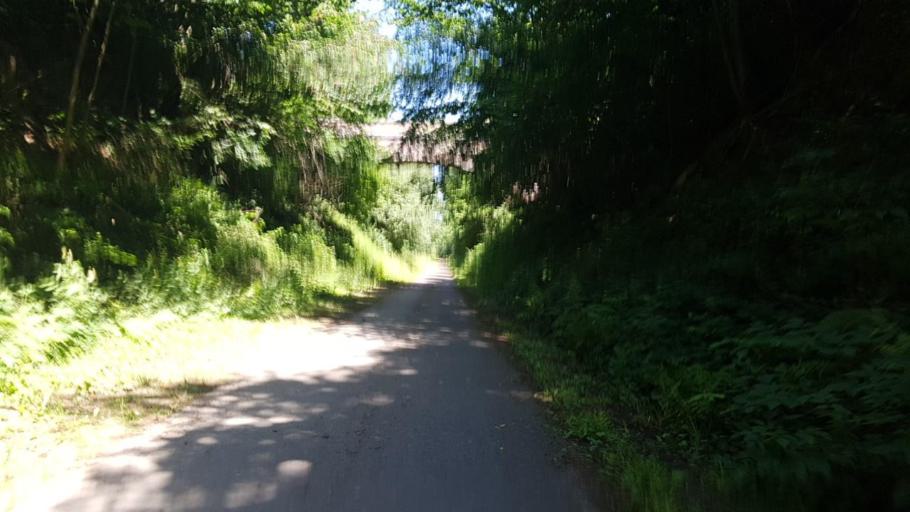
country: BE
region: Wallonia
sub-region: Province du Hainaut
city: Beaumont
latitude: 50.1984
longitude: 4.2279
